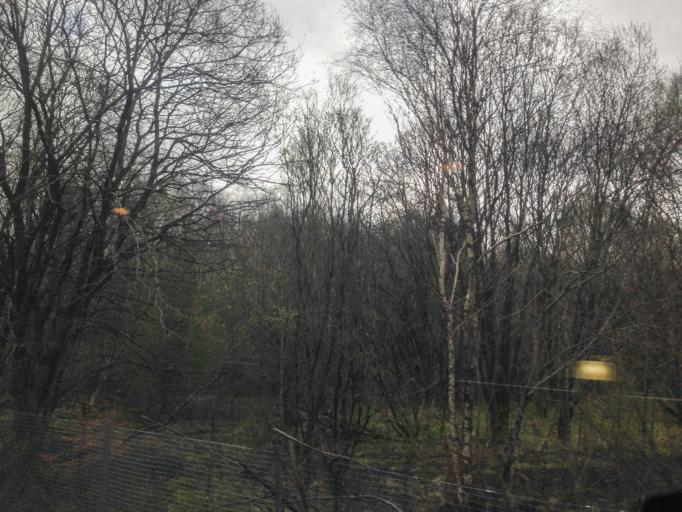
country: GB
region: Scotland
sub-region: Highland
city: Fort William
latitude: 56.8440
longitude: -5.1524
